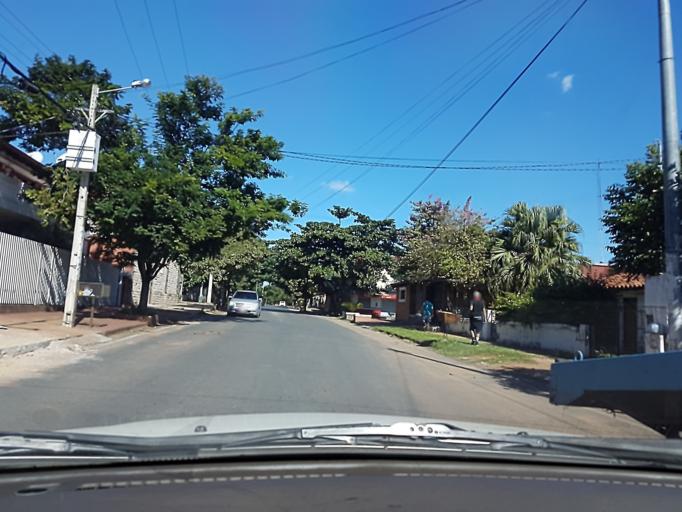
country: PY
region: Central
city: Lambare
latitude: -25.3245
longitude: -57.5848
